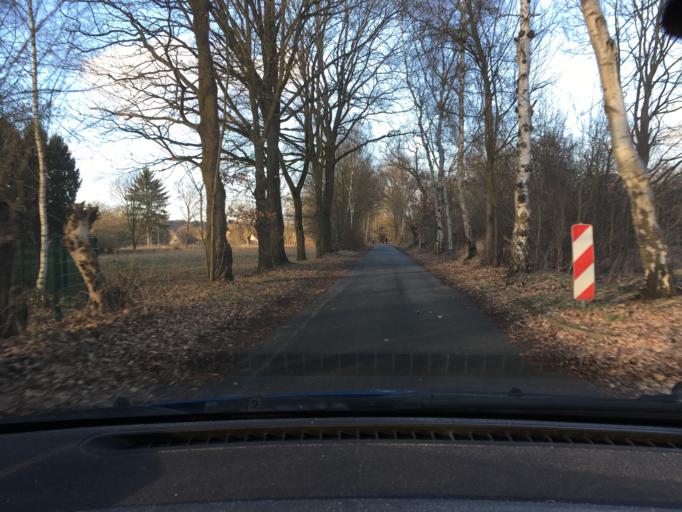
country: DE
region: Schleswig-Holstein
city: Witzeeze
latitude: 53.4531
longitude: 10.6254
